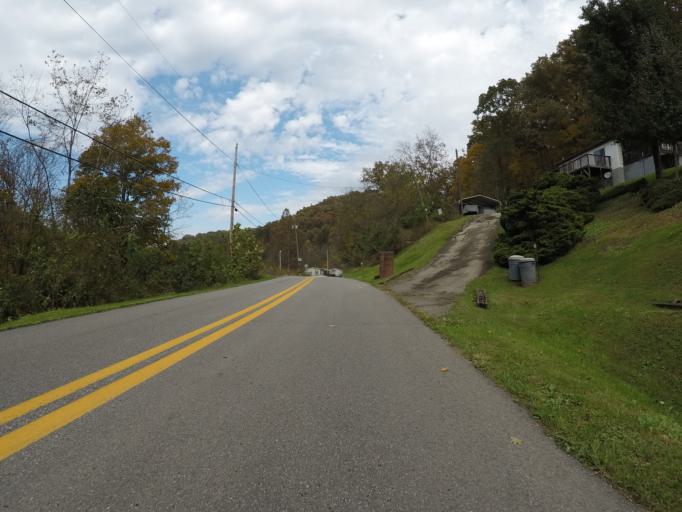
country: US
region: West Virginia
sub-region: Wayne County
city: Lavalette
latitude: 38.3431
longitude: -82.4499
